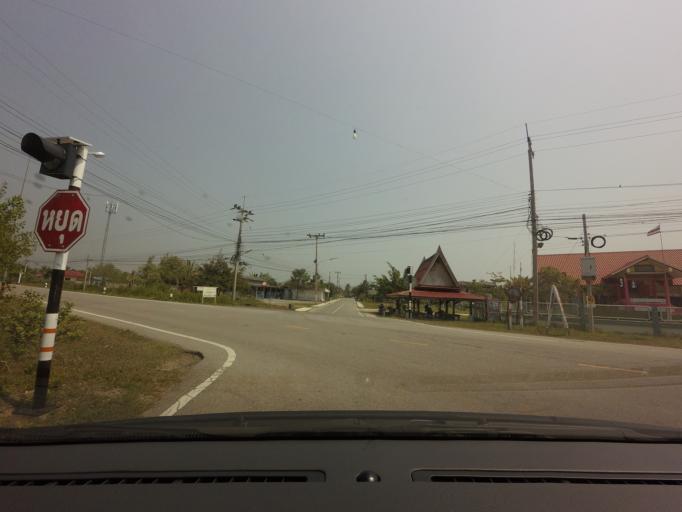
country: TH
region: Prachuap Khiri Khan
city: Kui Buri
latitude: 12.1364
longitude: 99.9637
